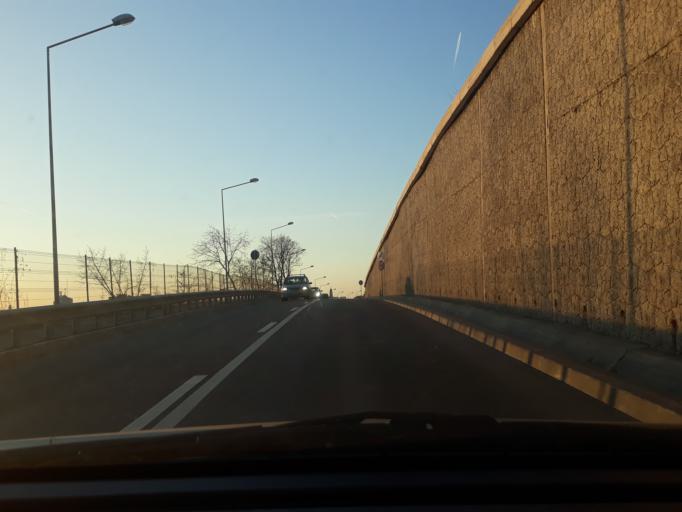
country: RO
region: Bihor
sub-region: Comuna Biharea
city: Oradea
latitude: 47.0540
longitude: 21.9538
